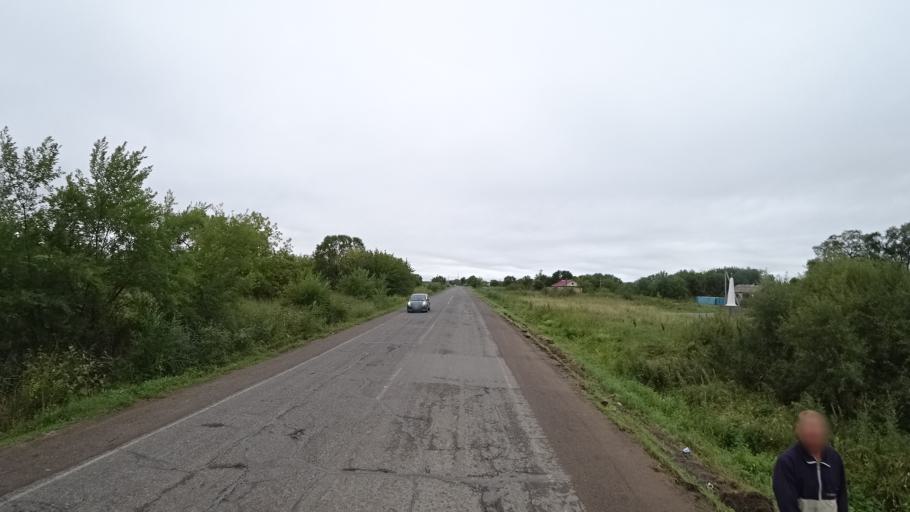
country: RU
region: Primorskiy
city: Monastyrishche
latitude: 44.1927
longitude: 132.4806
